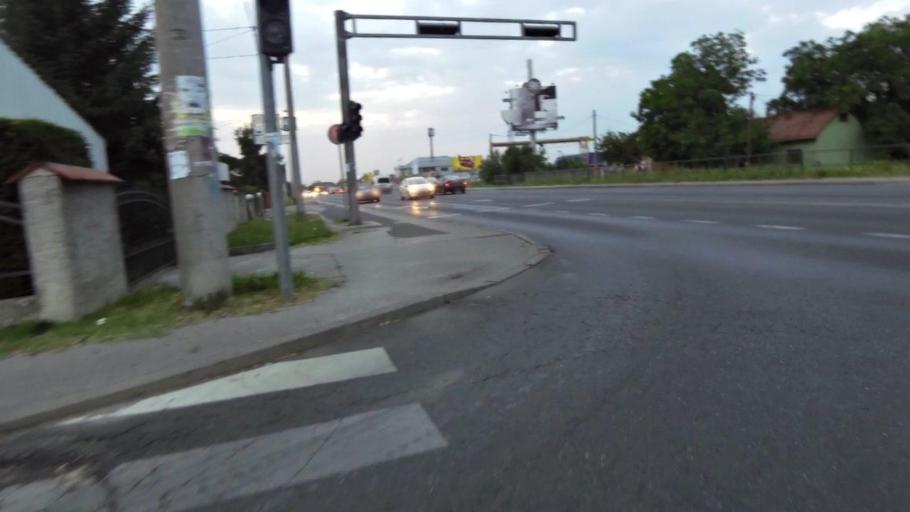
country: HR
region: Grad Zagreb
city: Dubrava
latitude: 45.8271
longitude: 16.0800
